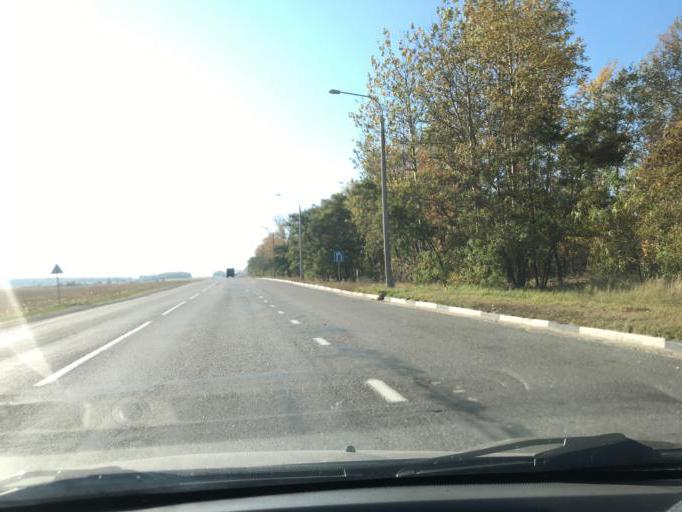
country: BY
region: Gomel
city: Rechytsa
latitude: 52.2663
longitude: 30.2541
